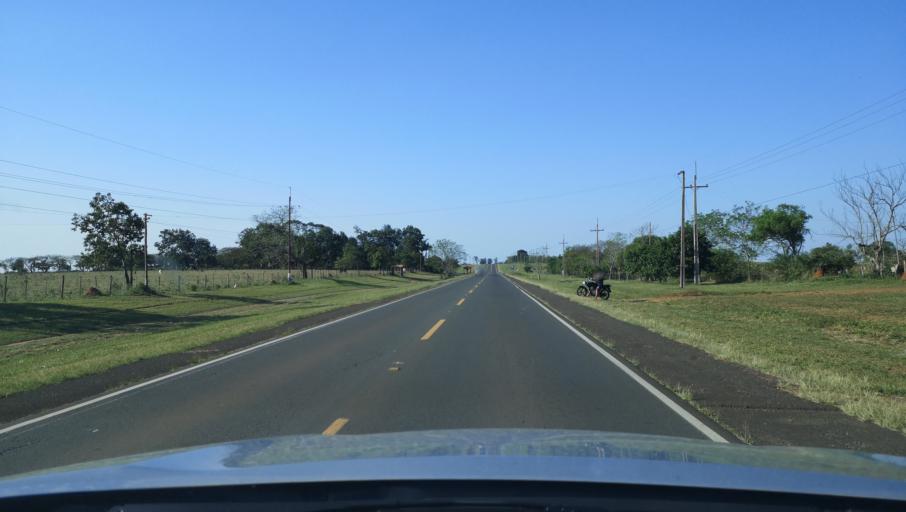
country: PY
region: Misiones
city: Santa Maria
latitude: -26.8178
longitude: -57.0250
